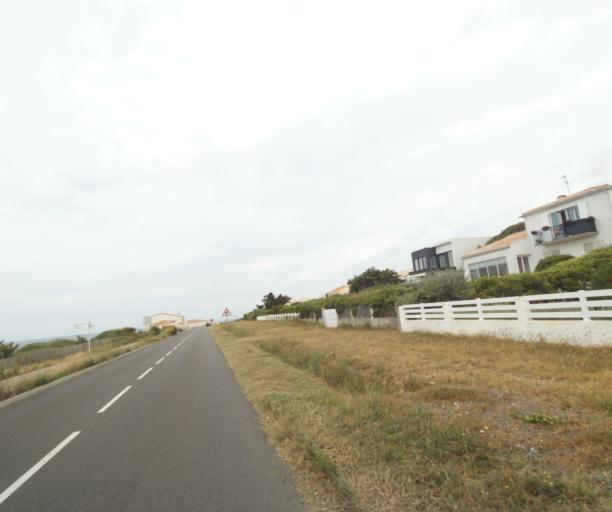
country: FR
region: Pays de la Loire
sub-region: Departement de la Vendee
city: Chateau-d'Olonne
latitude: 46.4663
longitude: -1.7331
